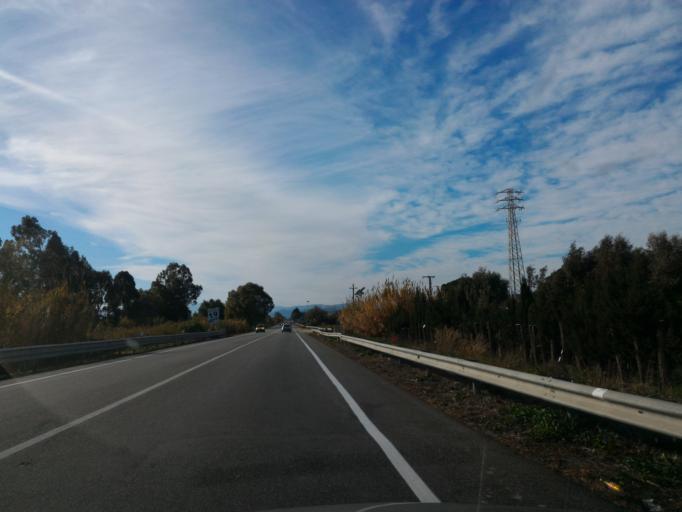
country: IT
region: Calabria
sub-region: Provincia di Catanzaro
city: Barone
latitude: 38.8621
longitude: 16.6799
